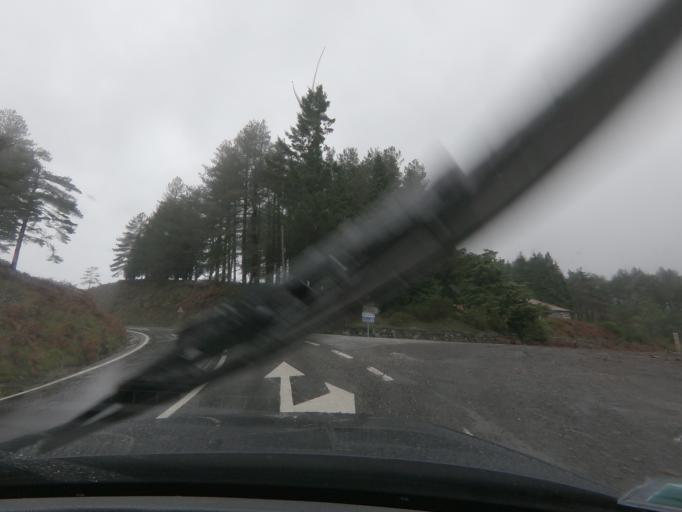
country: PT
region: Vila Real
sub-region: Mondim de Basto
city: Mondim de Basto
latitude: 41.3168
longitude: -7.8884
